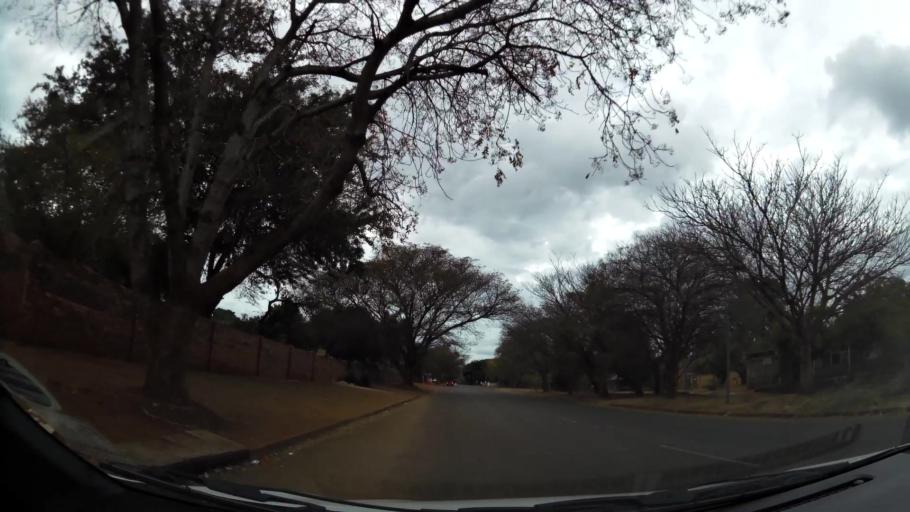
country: ZA
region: Limpopo
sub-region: Waterberg District Municipality
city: Mokopane
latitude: -24.1872
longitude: 28.9962
